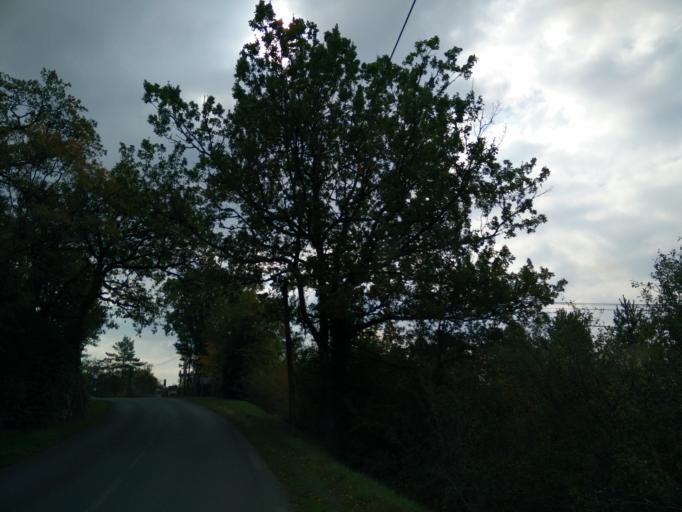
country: FR
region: Aquitaine
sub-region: Departement de la Dordogne
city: Montignac
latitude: 45.0542
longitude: 1.1648
